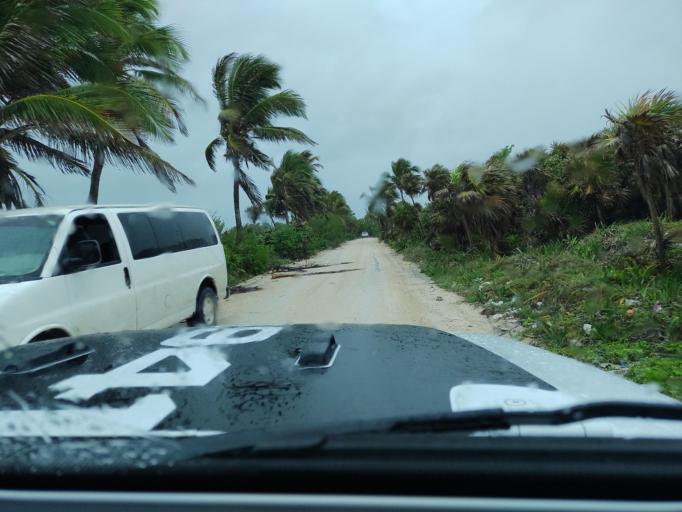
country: MX
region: Quintana Roo
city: Tulum
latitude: 19.9841
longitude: -87.4666
